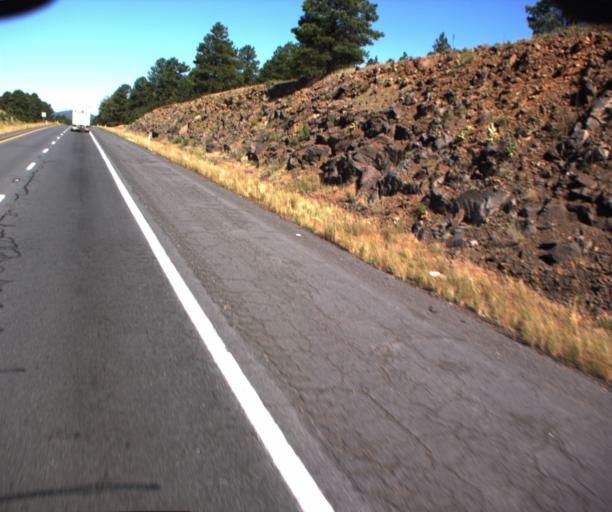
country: US
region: Arizona
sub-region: Coconino County
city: Parks
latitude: 35.2544
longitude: -112.0058
